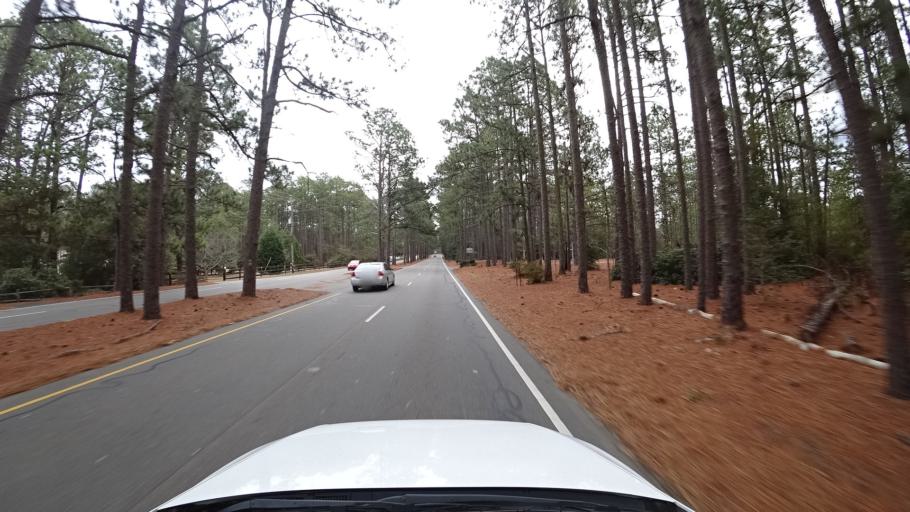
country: US
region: North Carolina
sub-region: Moore County
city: Southern Pines
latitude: 35.1986
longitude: -79.4132
